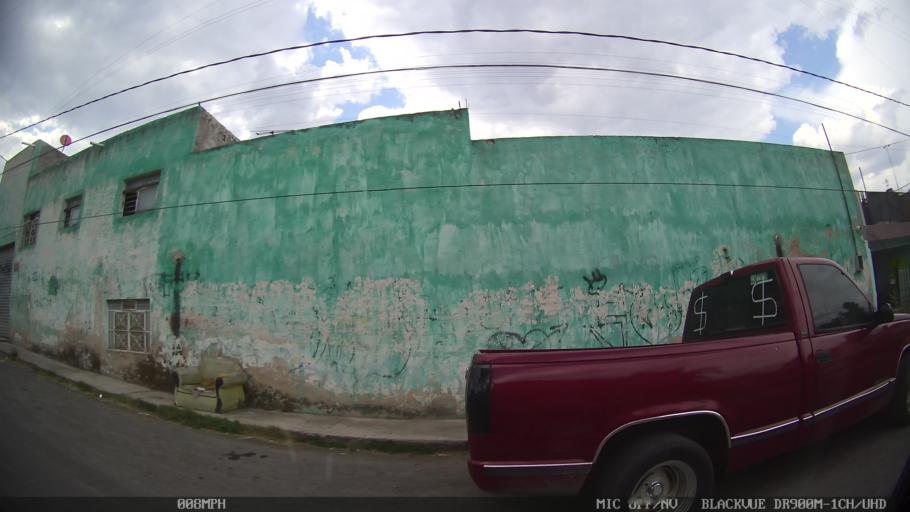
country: MX
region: Jalisco
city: Tlaquepaque
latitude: 20.6279
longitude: -103.2716
